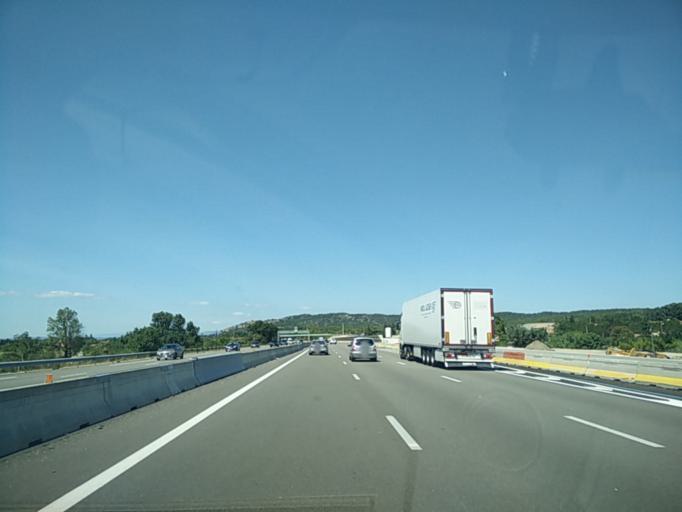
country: FR
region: Provence-Alpes-Cote d'Azur
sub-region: Departement du Vaucluse
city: Piolenc
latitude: 44.1803
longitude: 4.7538
